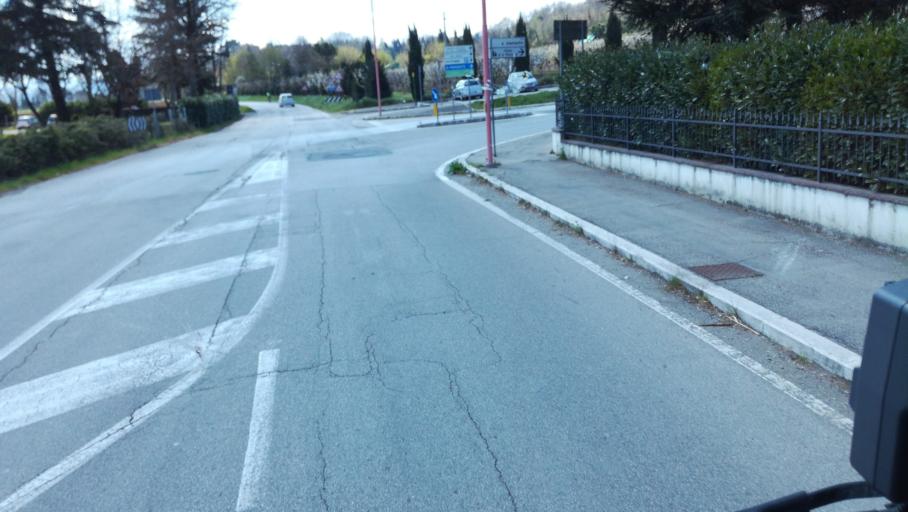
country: IT
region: Emilia-Romagna
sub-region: Forli-Cesena
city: Borello
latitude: 44.0859
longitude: 12.1900
